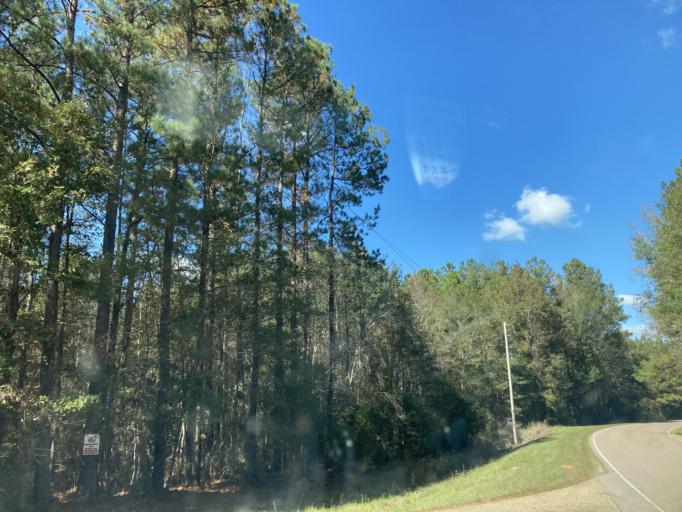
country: US
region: Mississippi
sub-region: Lamar County
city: Sumrall
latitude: 31.3100
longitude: -89.5424
